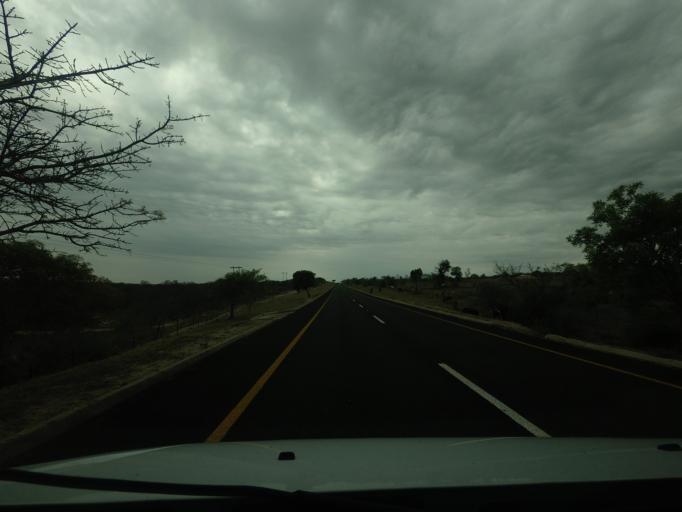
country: ZA
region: Limpopo
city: Thulamahashi
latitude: -24.5648
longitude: 31.1228
